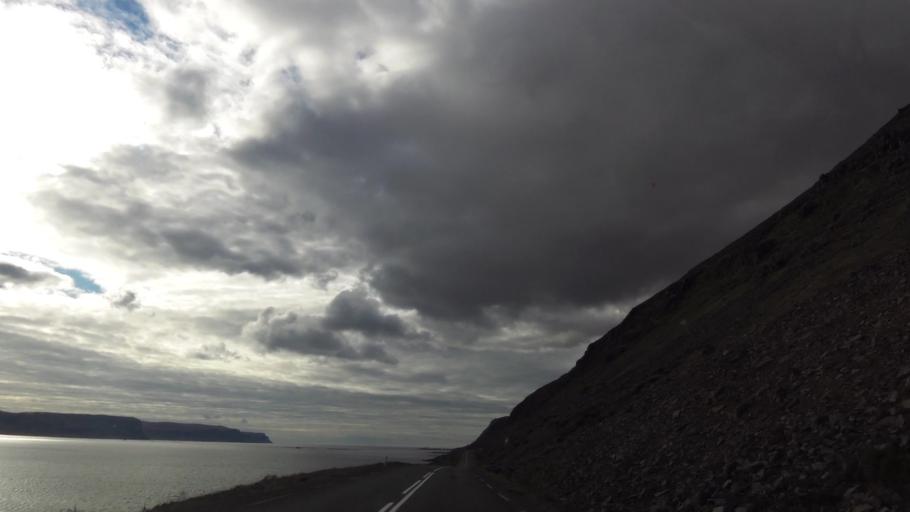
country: IS
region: West
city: Olafsvik
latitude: 65.5634
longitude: -23.9154
